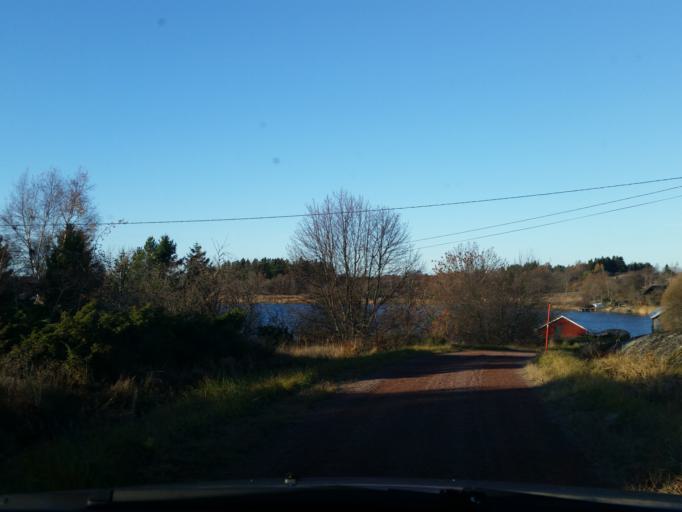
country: AX
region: Alands skaergard
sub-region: Braendoe
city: Braendoe
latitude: 60.4528
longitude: 20.9359
